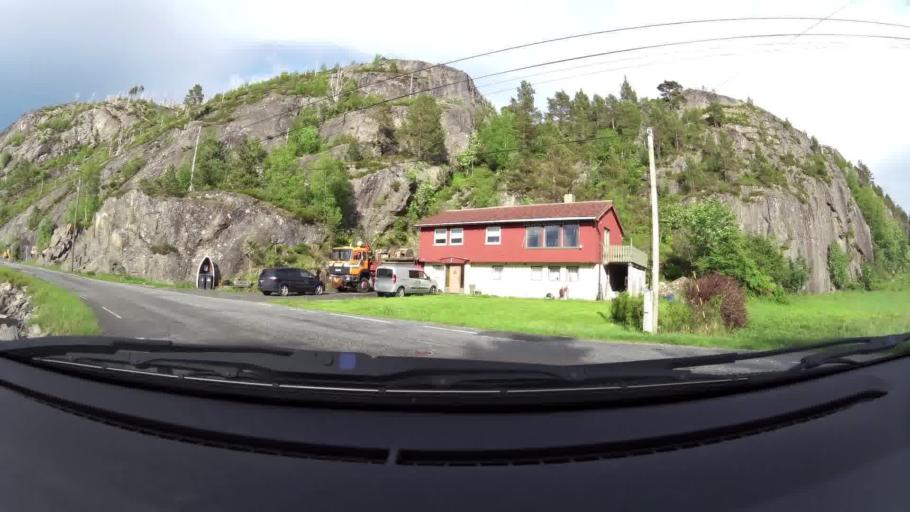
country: NO
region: More og Romsdal
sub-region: Kristiansund
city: Kristiansund
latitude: 63.0511
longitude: 7.7089
